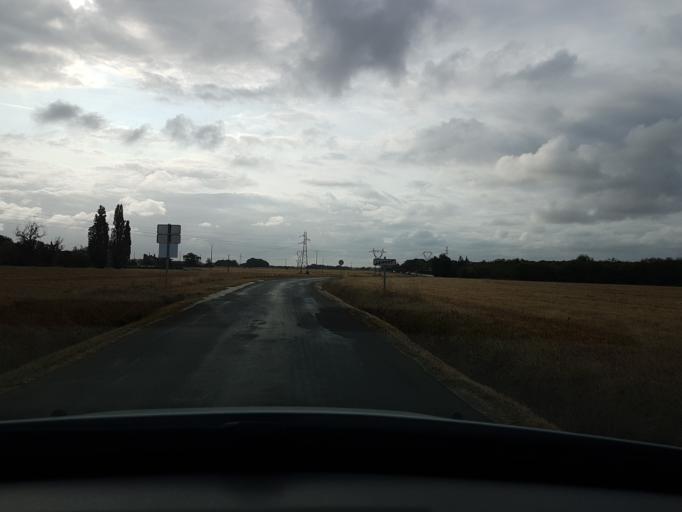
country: FR
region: Centre
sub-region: Departement d'Indre-et-Loire
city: Larcay
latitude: 47.3460
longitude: 0.7790
